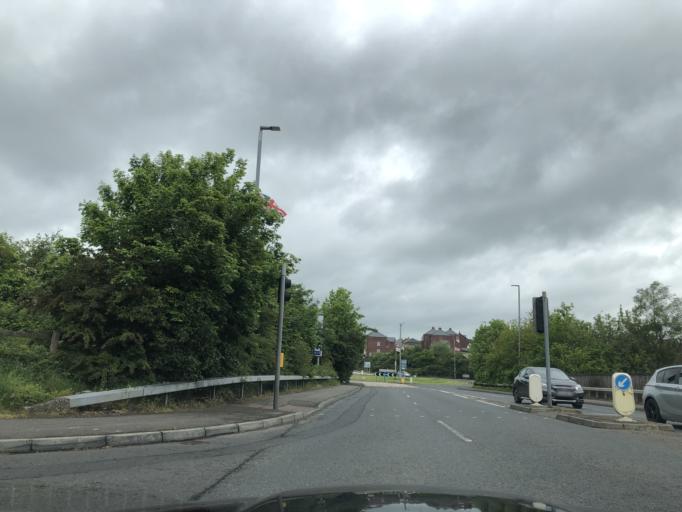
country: GB
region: Northern Ireland
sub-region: Lisburn District
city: Lisburn
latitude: 54.5274
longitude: -6.0729
